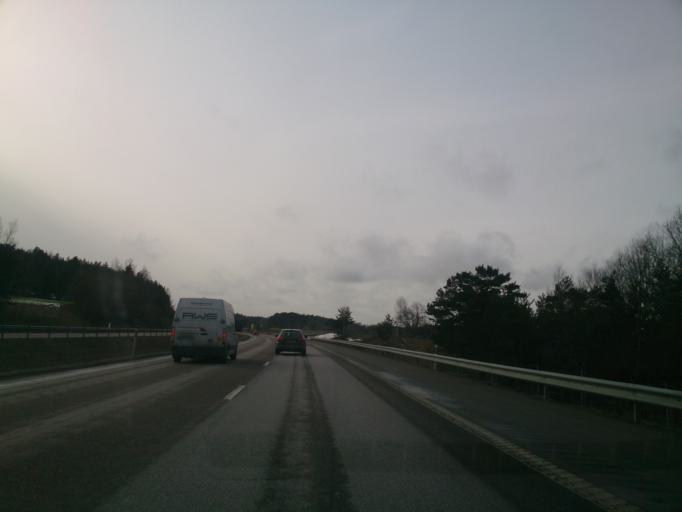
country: SE
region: Soedermanland
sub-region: Gnesta Kommun
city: Gnesta
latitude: 58.8841
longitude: 17.2499
